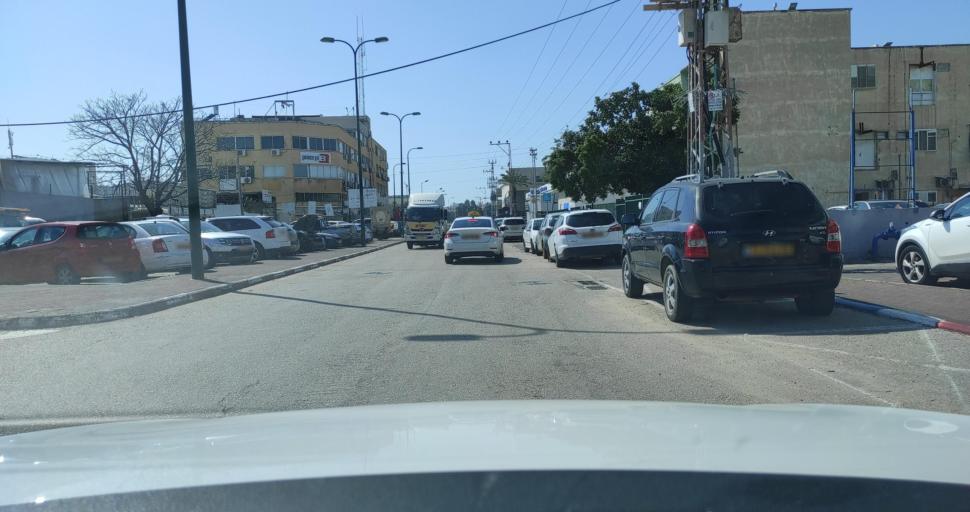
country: IL
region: Central District
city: Bet Yizhaq
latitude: 32.3212
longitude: 34.8761
